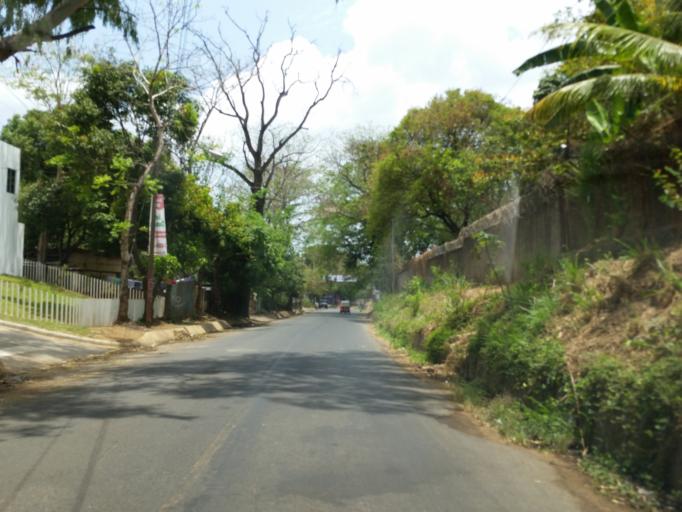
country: NI
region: Managua
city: Managua
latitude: 12.0869
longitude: -86.2422
